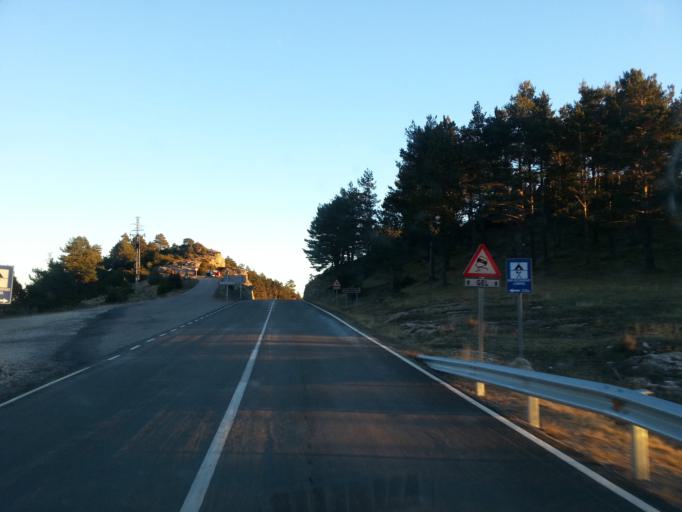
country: ES
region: Catalonia
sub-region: Provincia de Lleida
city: Olius
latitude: 42.1384
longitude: 1.5395
